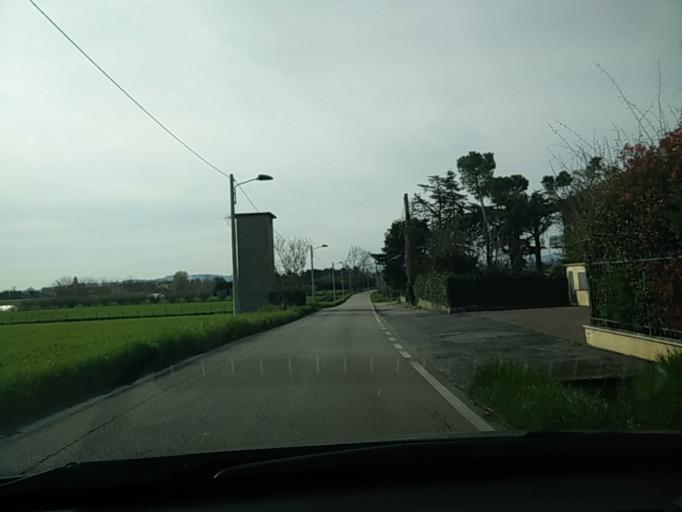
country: IT
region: Emilia-Romagna
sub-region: Provincia di Rimini
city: Santa Giustina
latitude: 44.0787
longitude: 12.5058
